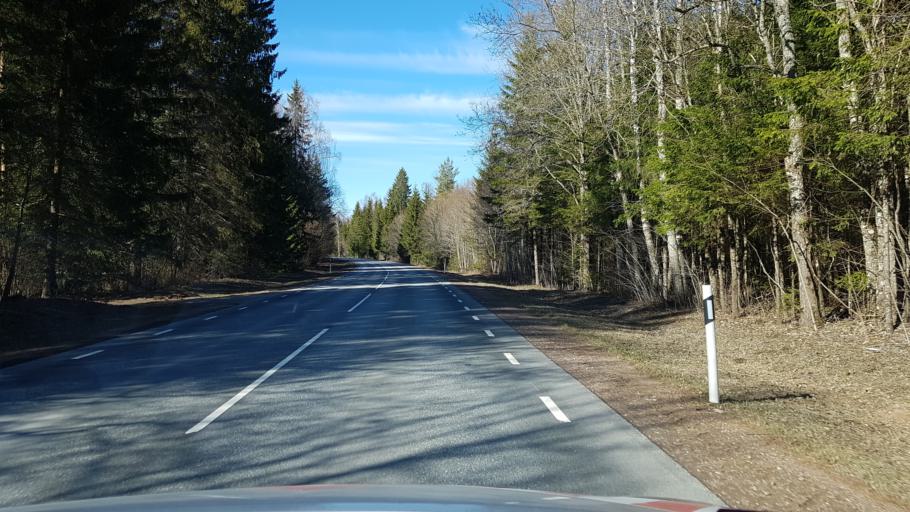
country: EE
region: Laeaene-Virumaa
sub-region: Kadrina vald
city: Kadrina
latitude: 59.3871
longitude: 26.0168
